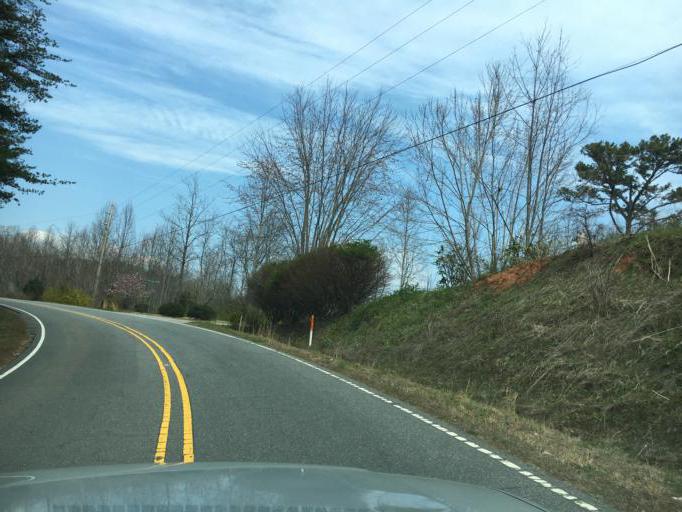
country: US
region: North Carolina
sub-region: Rutherford County
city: Lake Lure
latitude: 35.4794
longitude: -82.1307
